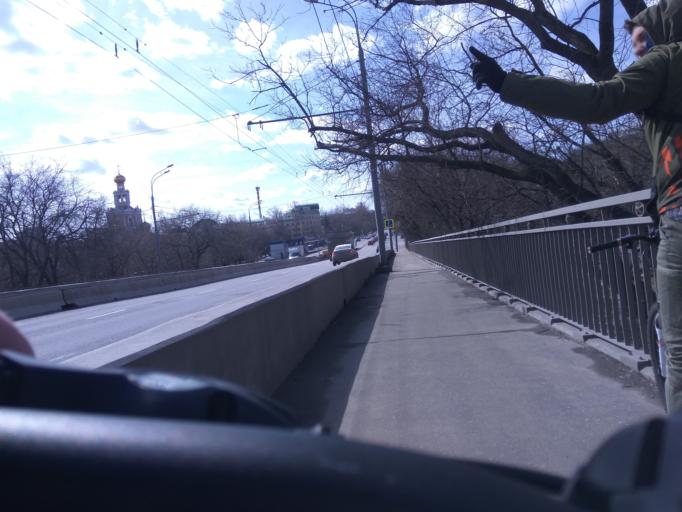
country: RU
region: Moskovskaya
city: Fili
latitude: 55.7524
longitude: 37.5124
